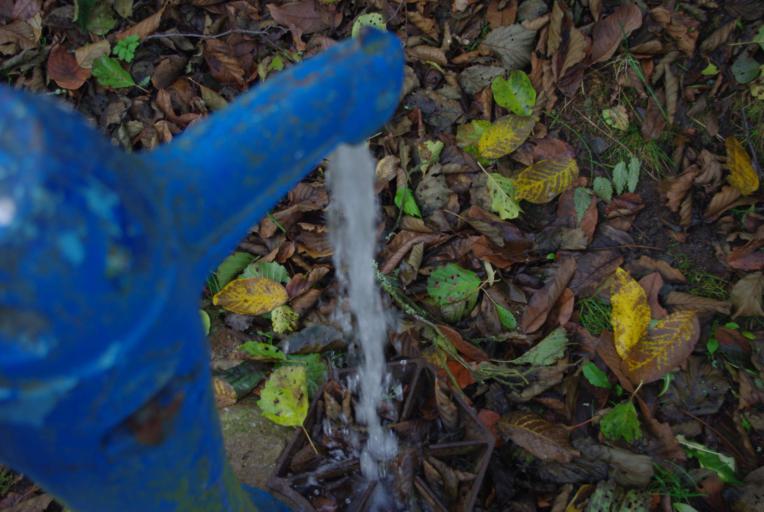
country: HU
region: Borsod-Abauj-Zemplen
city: Sarospatak
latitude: 48.4274
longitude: 21.4953
